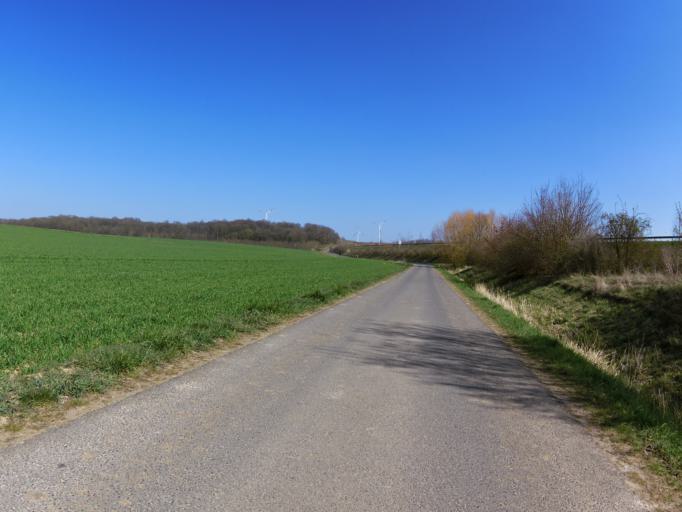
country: DE
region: Bavaria
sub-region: Regierungsbezirk Unterfranken
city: Biebelried
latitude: 49.7684
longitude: 10.0777
